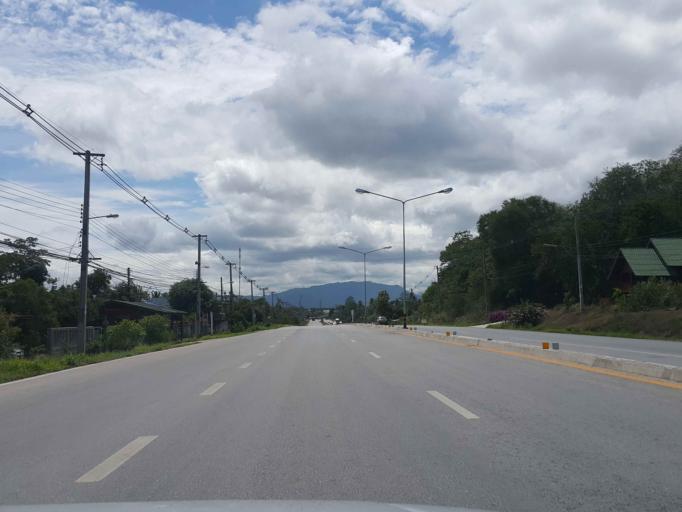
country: TH
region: Tak
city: Tak
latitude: 16.8871
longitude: 99.1758
